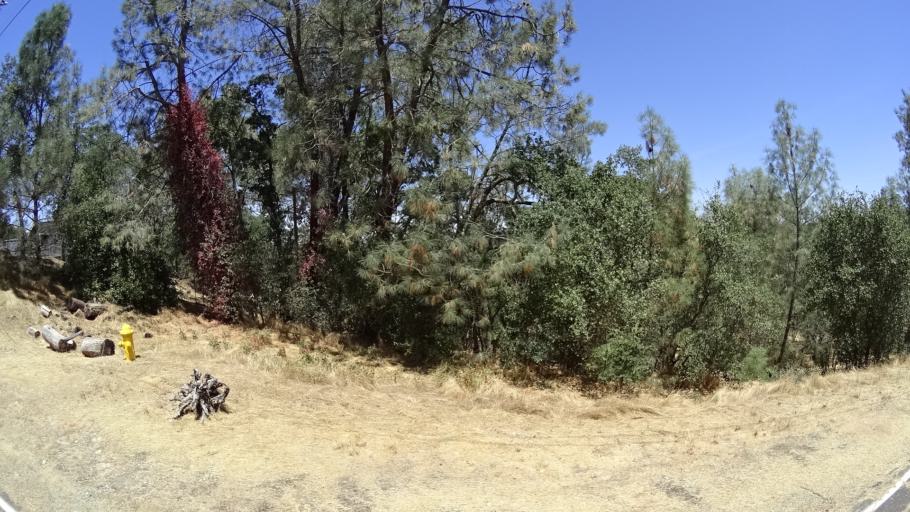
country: US
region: California
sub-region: Calaveras County
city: Rancho Calaveras
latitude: 38.1260
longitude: -120.8711
